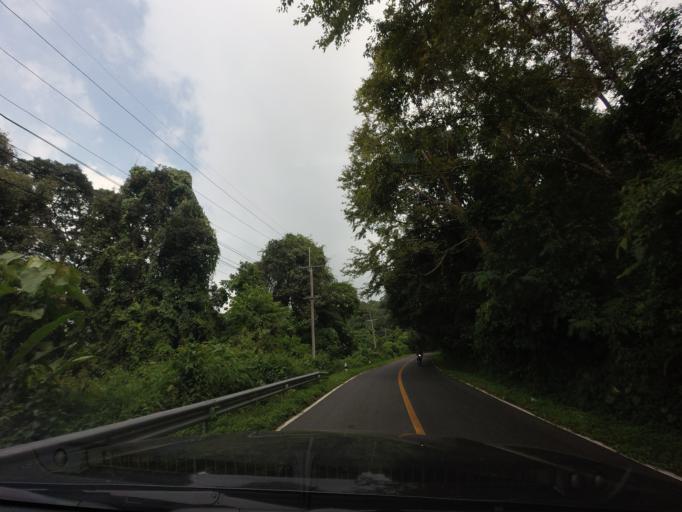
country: TH
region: Nan
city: Pua
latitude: 19.1887
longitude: 101.0268
